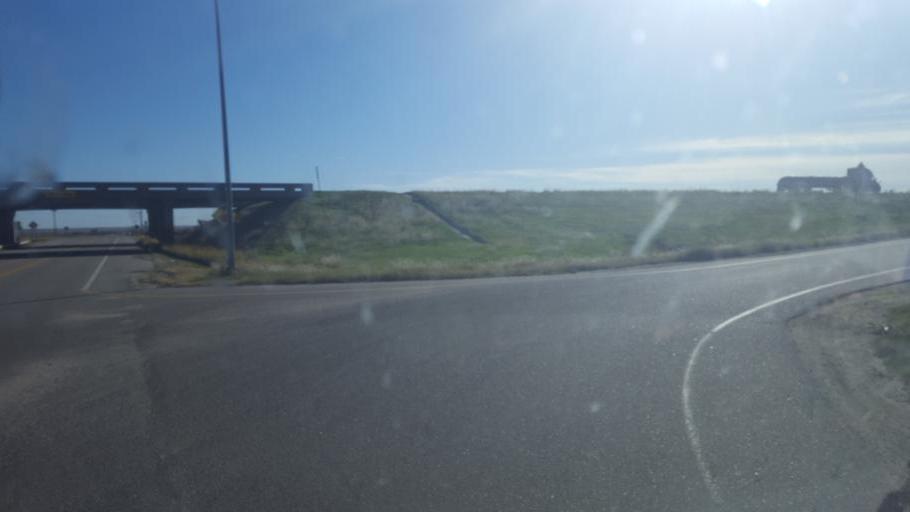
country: US
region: Kansas
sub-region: Russell County
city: Russell
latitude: 38.8584
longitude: -98.7067
